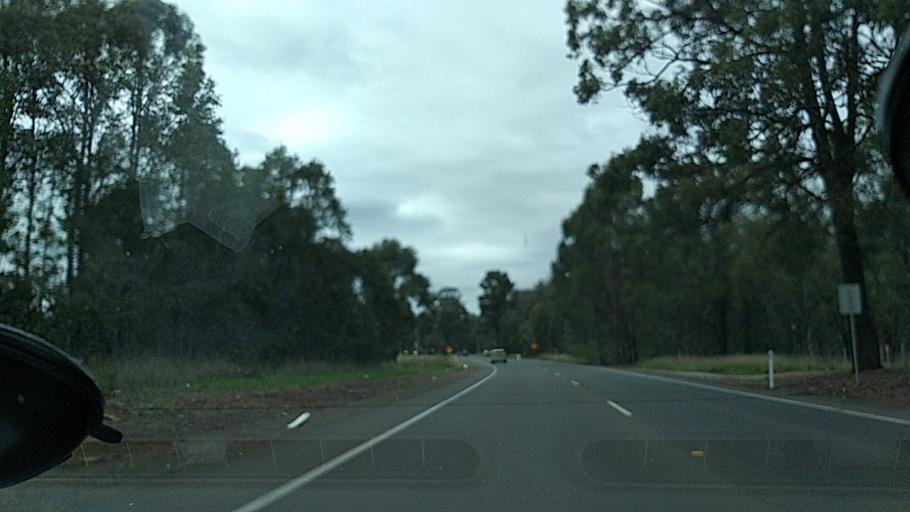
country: AU
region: New South Wales
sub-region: Penrith Municipality
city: Werrington Downs
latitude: -33.6951
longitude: 150.7277
